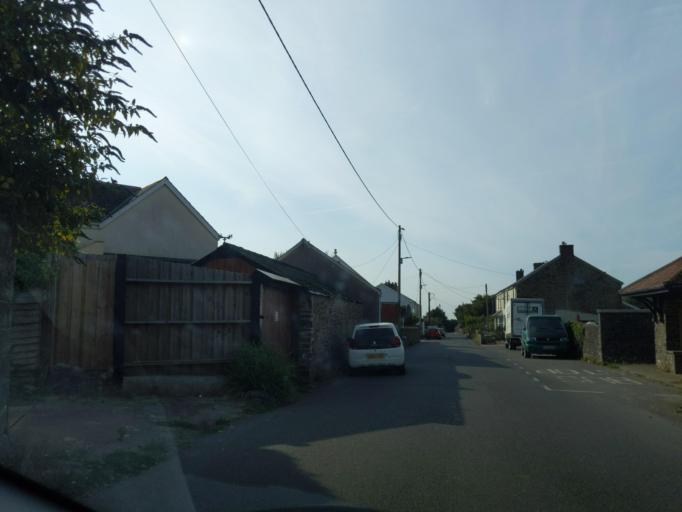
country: GB
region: England
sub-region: Devon
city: Winkleigh
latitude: 50.9672
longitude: -3.9941
